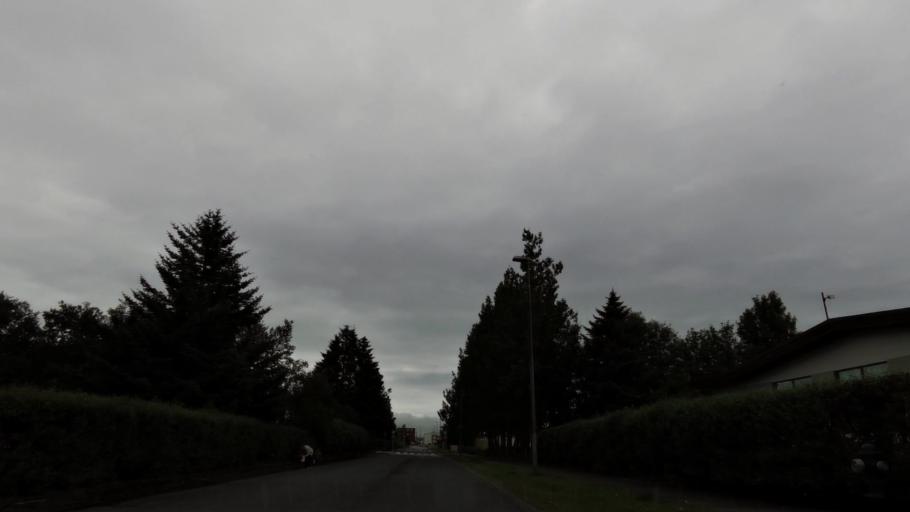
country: IS
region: Capital Region
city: Hafnarfjoerdur
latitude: 64.0827
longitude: -21.9602
